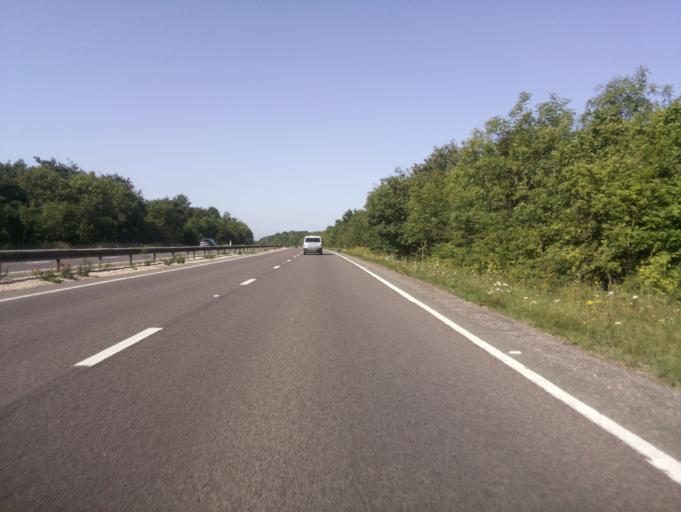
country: GB
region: England
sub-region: Oxfordshire
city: Witney
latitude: 51.7848
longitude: -1.4544
